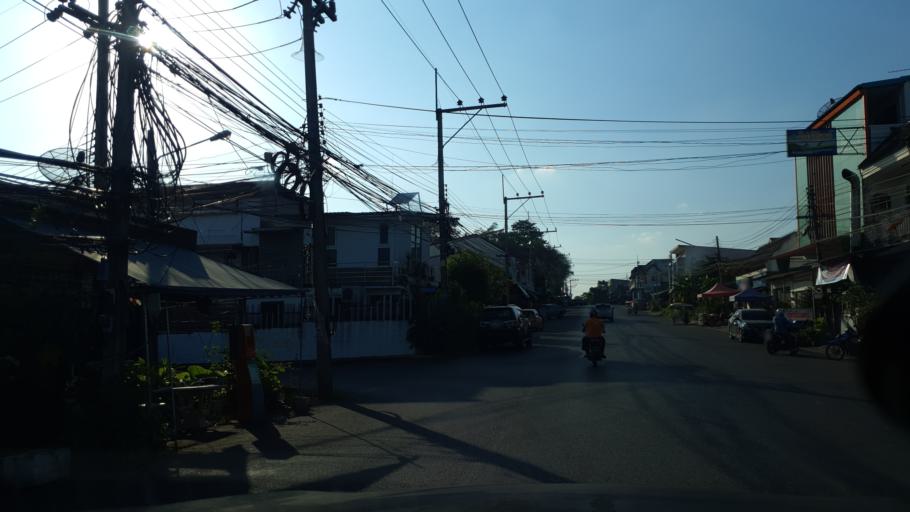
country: TH
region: Krabi
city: Krabi
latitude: 8.0807
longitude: 98.9125
